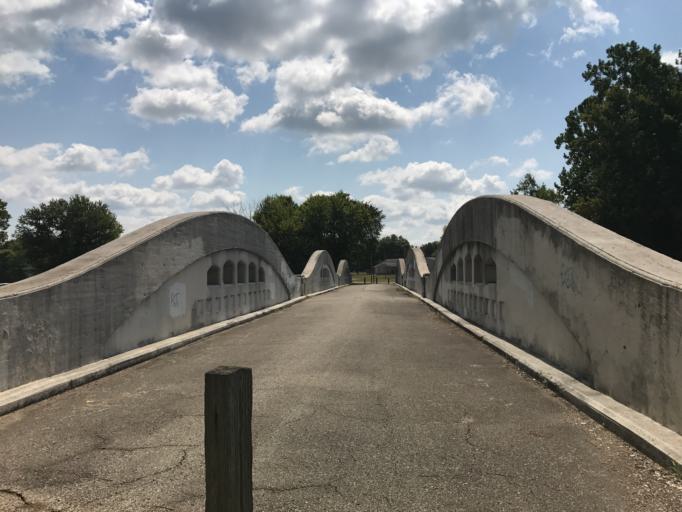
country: US
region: Michigan
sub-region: Saint Joseph County
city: Constantine
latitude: 41.8004
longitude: -85.7573
